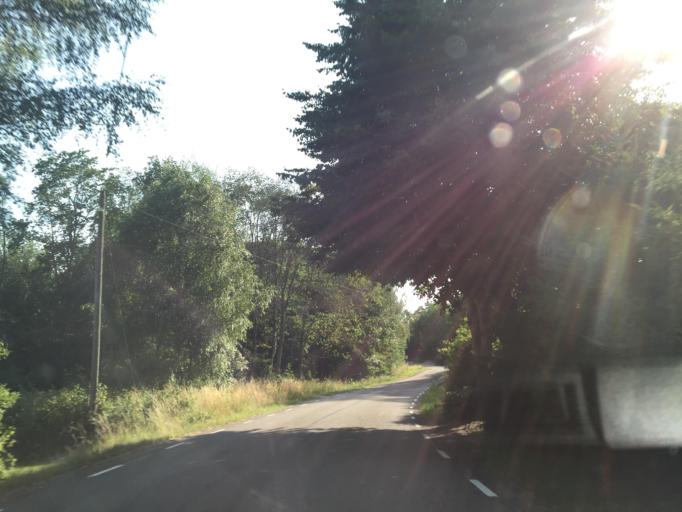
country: SE
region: Vaestra Goetaland
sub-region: Trollhattan
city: Trollhattan
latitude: 58.2710
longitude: 12.2476
